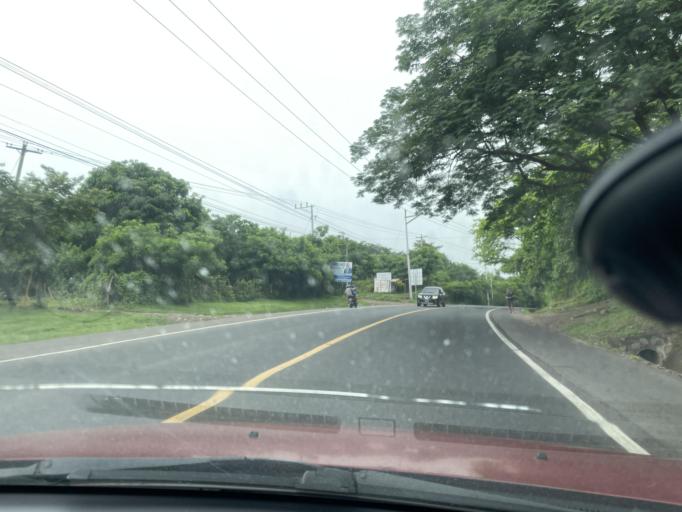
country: SV
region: San Miguel
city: San Miguel
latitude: 13.5238
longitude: -88.1451
